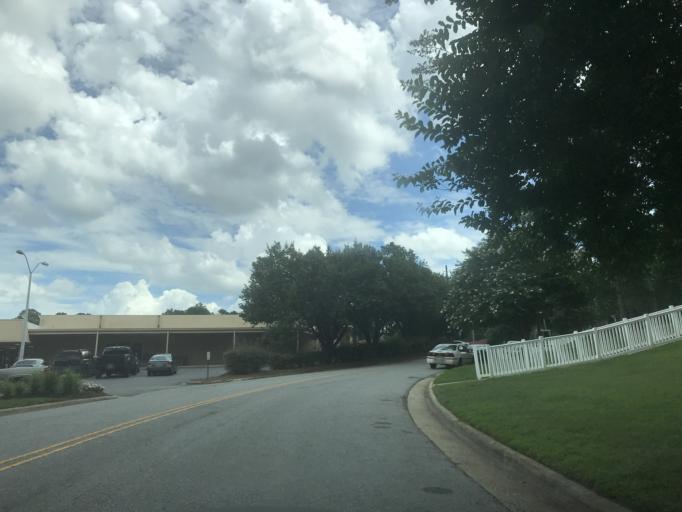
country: US
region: North Carolina
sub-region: Wake County
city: Raleigh
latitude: 35.8362
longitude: -78.6163
